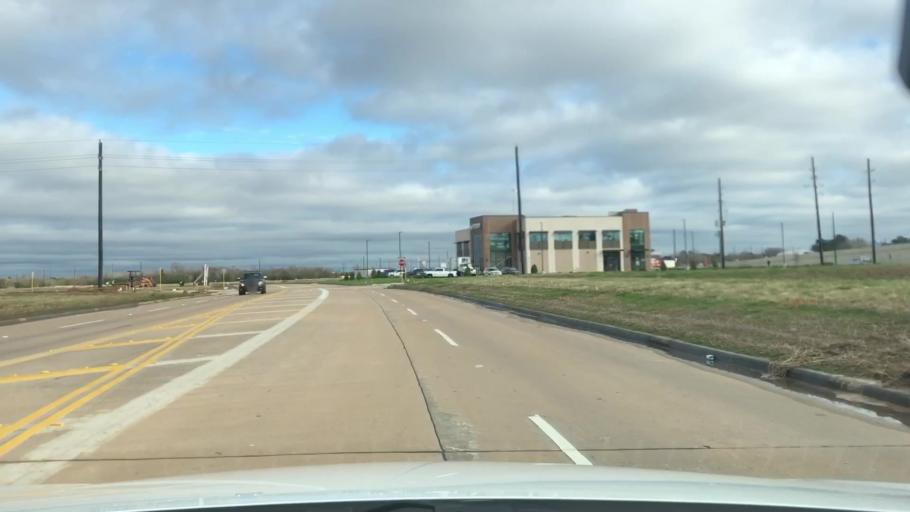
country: US
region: Texas
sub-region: Fort Bend County
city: Cinco Ranch
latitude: 29.7874
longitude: -95.7718
